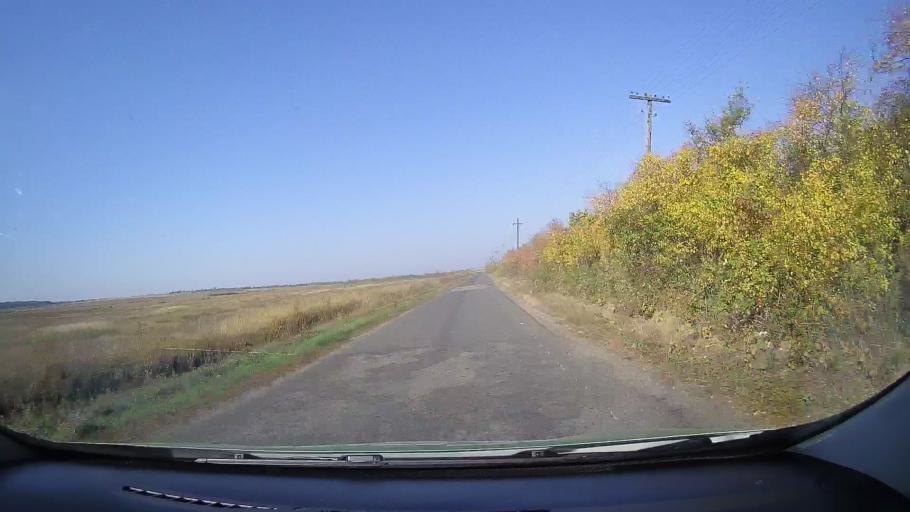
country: RO
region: Satu Mare
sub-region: Oras Tasnad
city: Tasnad
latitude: 47.4786
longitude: 22.5473
